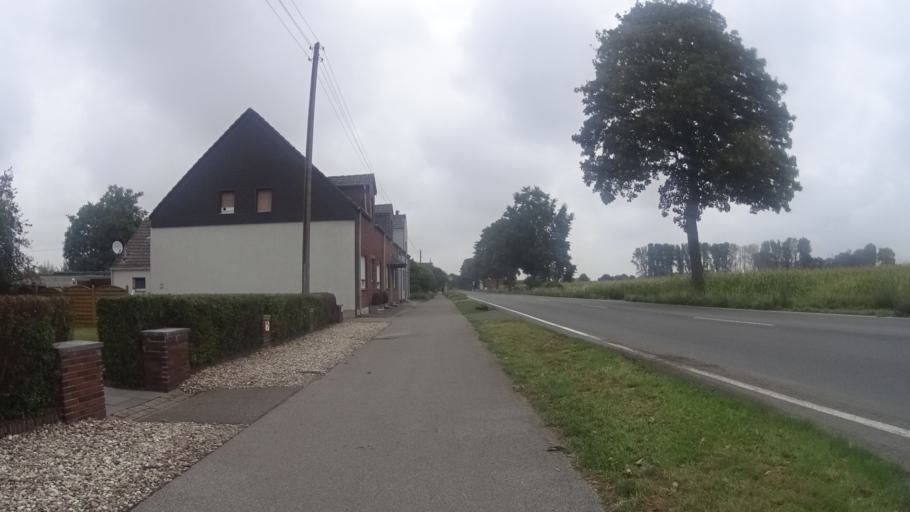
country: DE
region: North Rhine-Westphalia
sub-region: Regierungsbezirk Dusseldorf
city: Alpen
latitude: 51.6195
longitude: 6.5686
